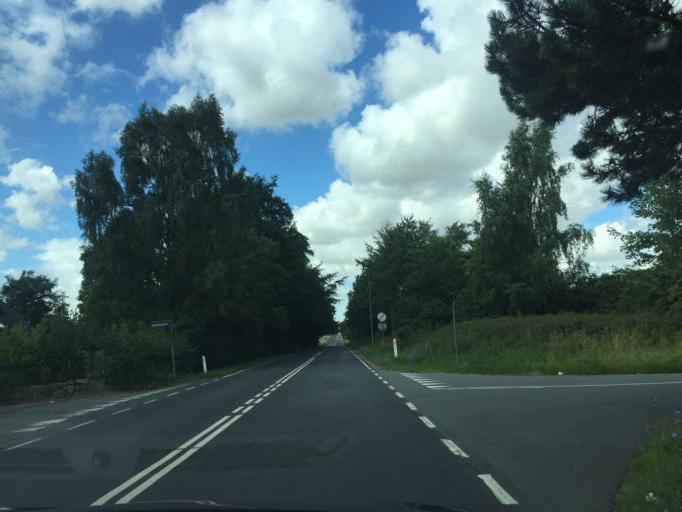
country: DK
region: South Denmark
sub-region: Odense Kommune
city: Stige
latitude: 55.4531
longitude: 10.3702
